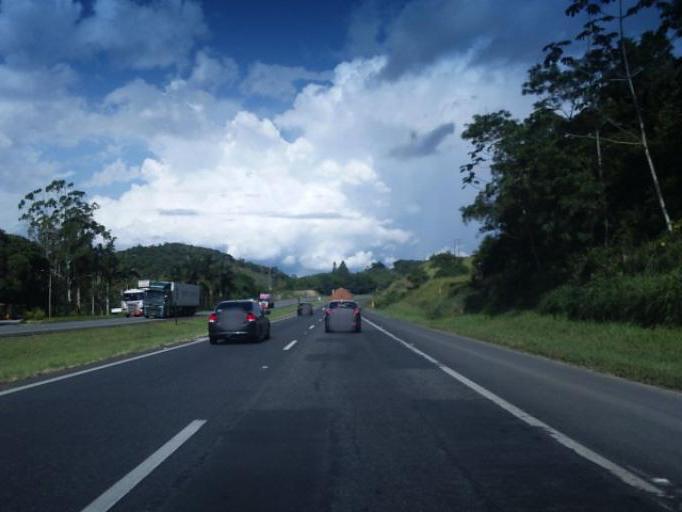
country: BR
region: Sao Paulo
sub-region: Juquia
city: Juquia
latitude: -24.3551
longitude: -47.6765
